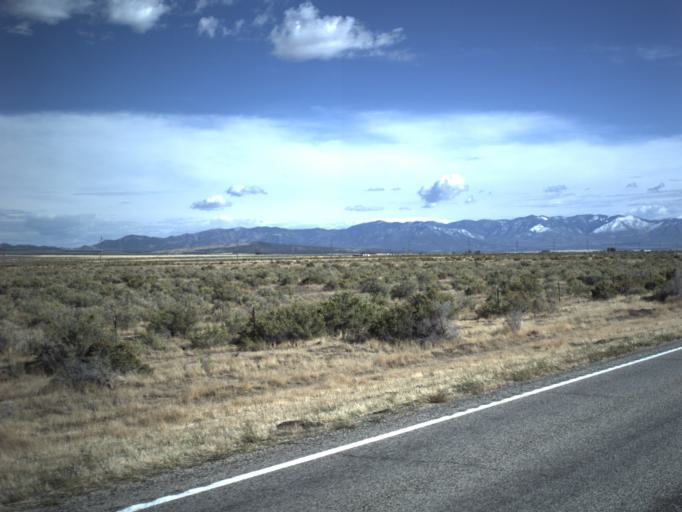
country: US
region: Utah
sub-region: Millard County
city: Delta
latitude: 39.2452
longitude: -112.4361
